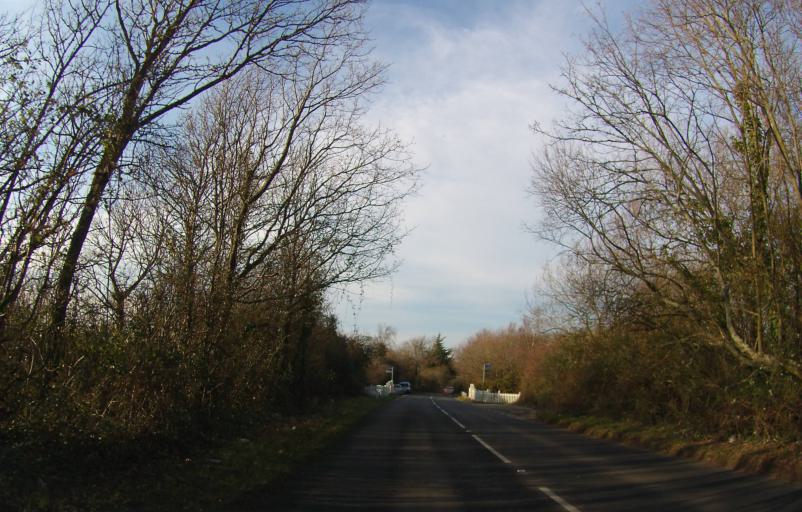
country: GB
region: England
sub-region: Isle of Wight
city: Newport
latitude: 50.7202
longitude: -1.2506
